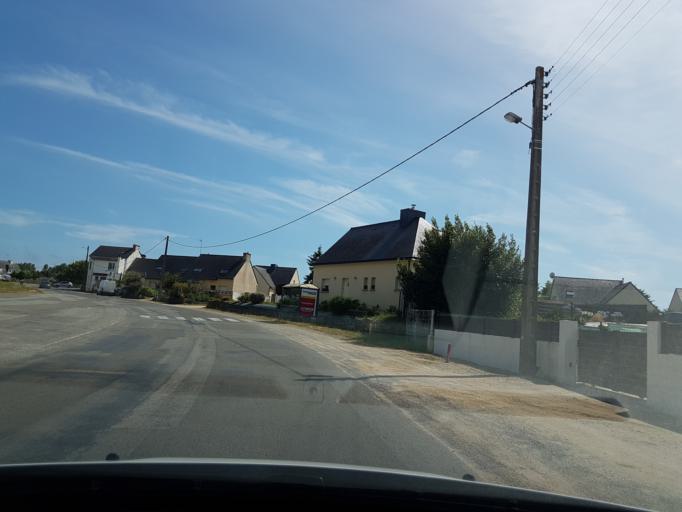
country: FR
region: Brittany
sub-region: Departement du Morbihan
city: Etel
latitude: 47.6699
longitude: -3.2212
